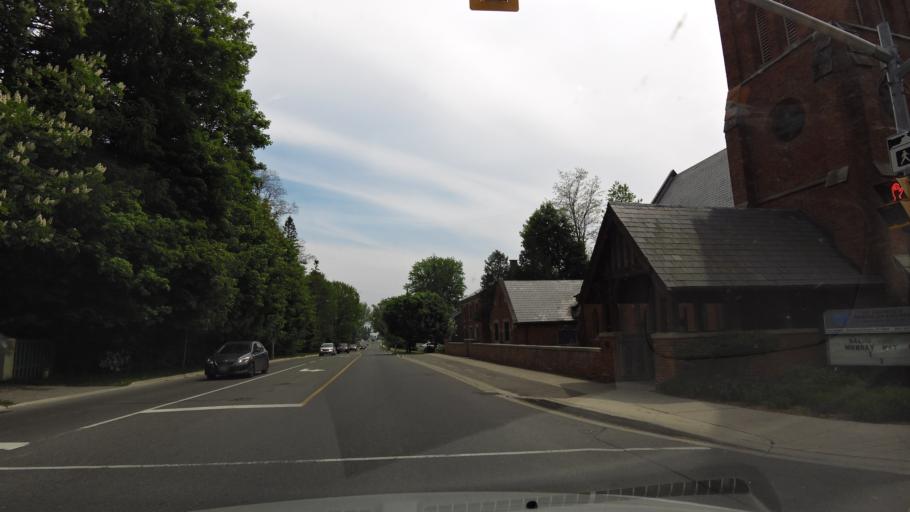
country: CA
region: Ontario
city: Oshawa
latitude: 43.9144
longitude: -78.5875
